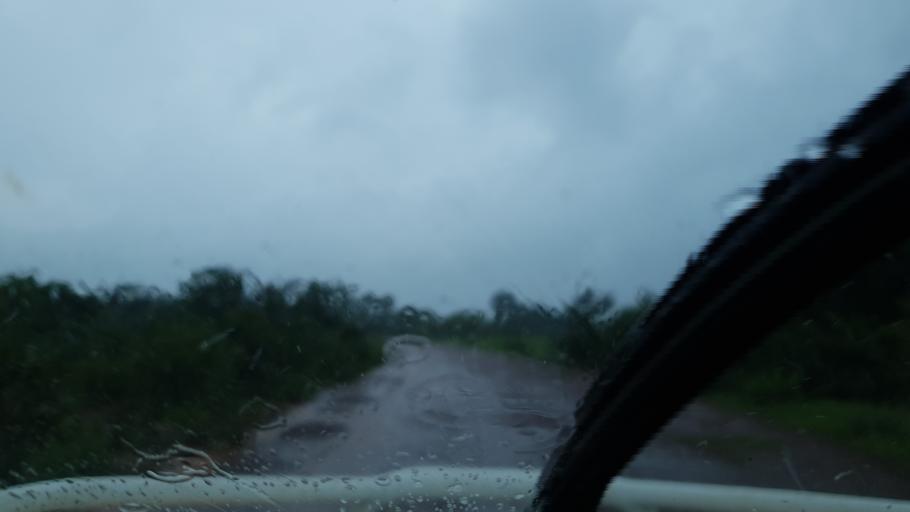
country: ML
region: Sikasso
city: Kolondieba
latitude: 11.6064
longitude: -6.6751
